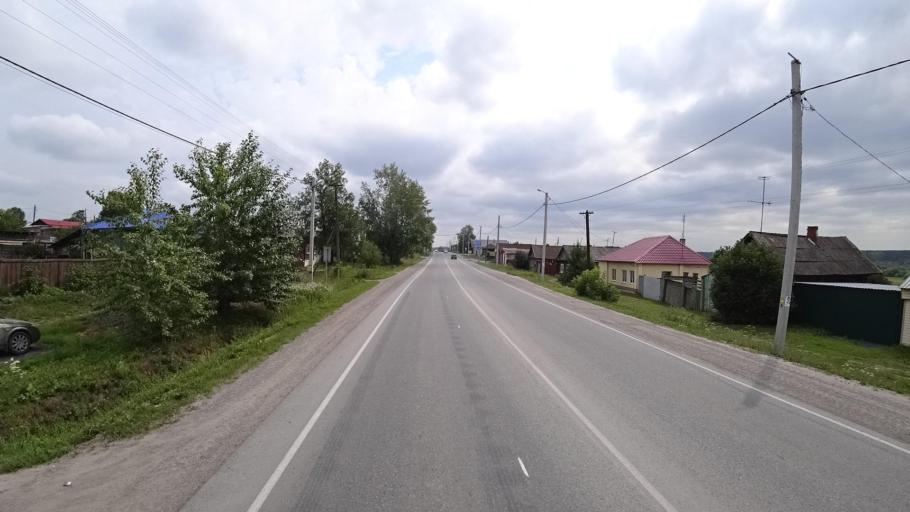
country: RU
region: Sverdlovsk
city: Kamyshlov
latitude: 56.8475
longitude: 62.6627
